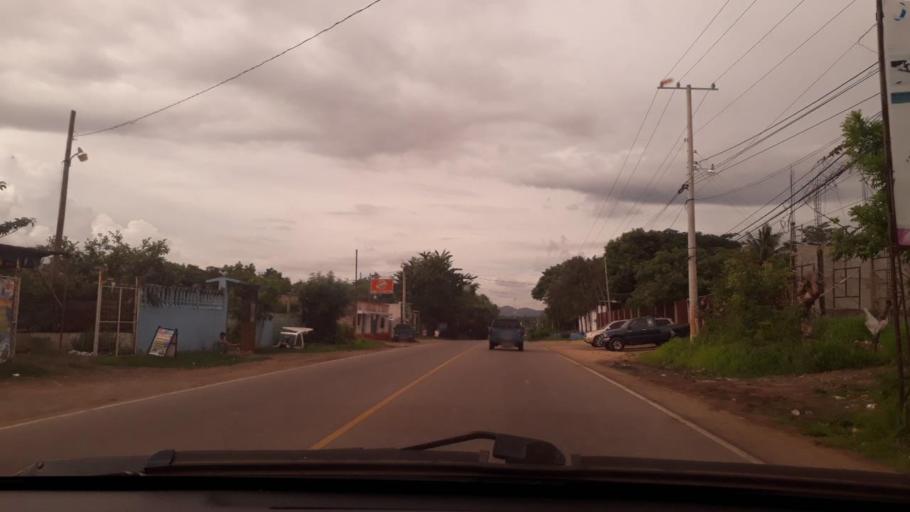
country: GT
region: Jutiapa
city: Jutiapa
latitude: 14.3059
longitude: -89.8704
